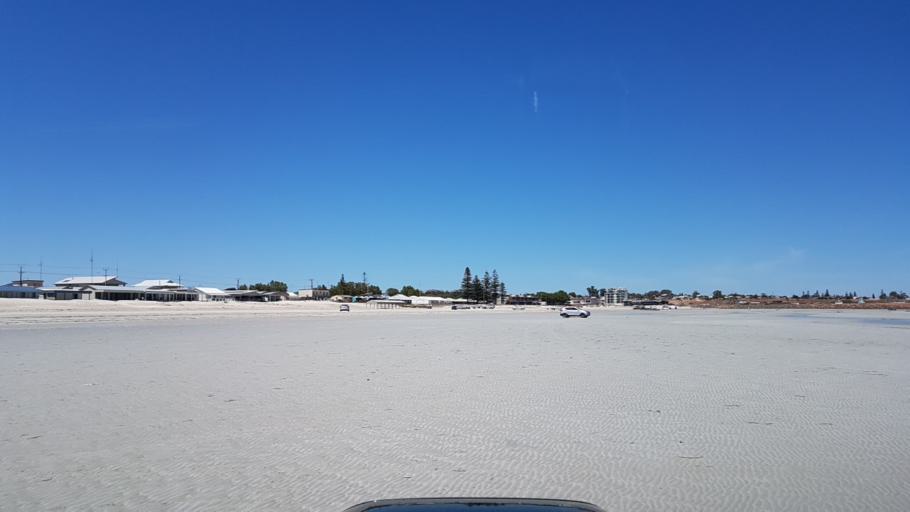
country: AU
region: South Australia
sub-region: Copper Coast
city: Wallaroo
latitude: -33.9157
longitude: 137.6303
